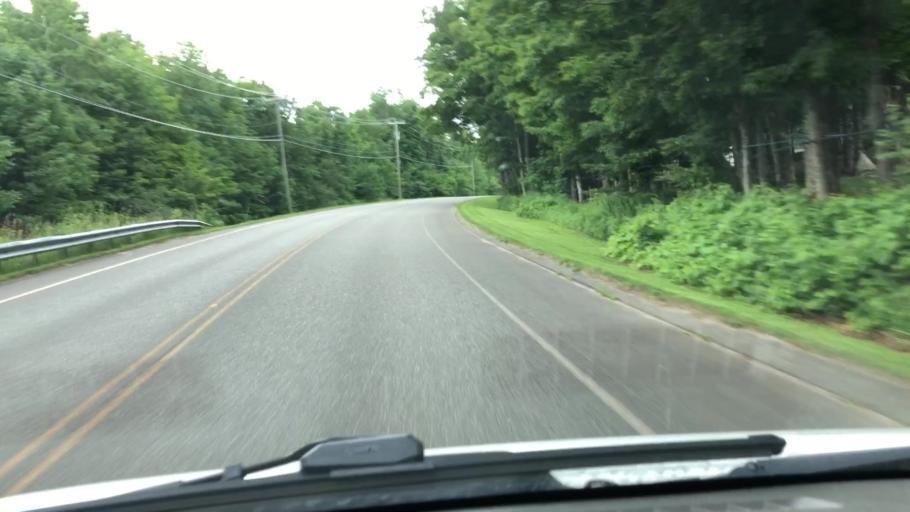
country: US
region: Massachusetts
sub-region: Berkshire County
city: Adams
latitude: 42.5424
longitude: -73.0534
